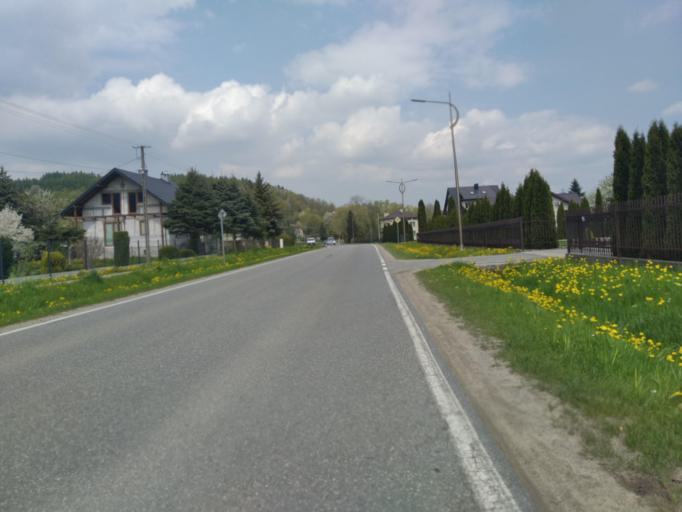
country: PL
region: Subcarpathian Voivodeship
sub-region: Powiat krosnienski
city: Rymanow
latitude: 49.5593
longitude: 21.8567
